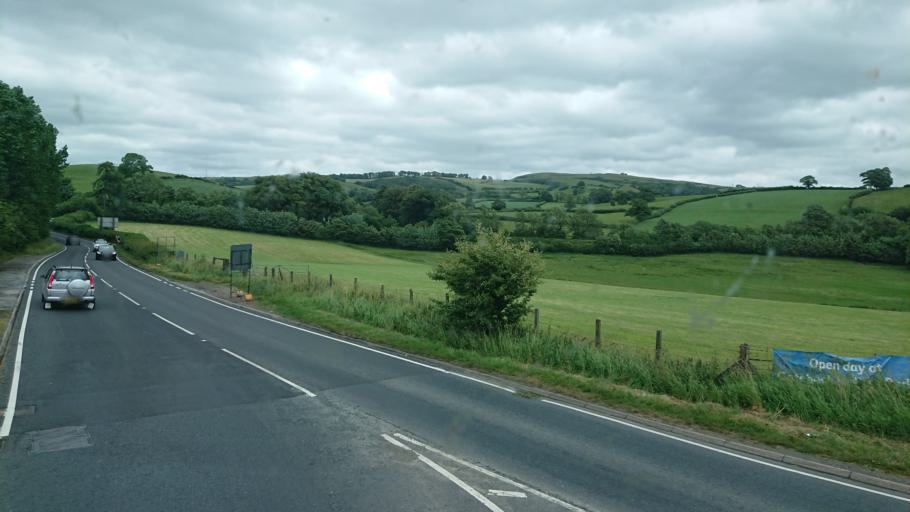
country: GB
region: England
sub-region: Cumbria
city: Milnthorpe
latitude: 54.2353
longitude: -2.7125
